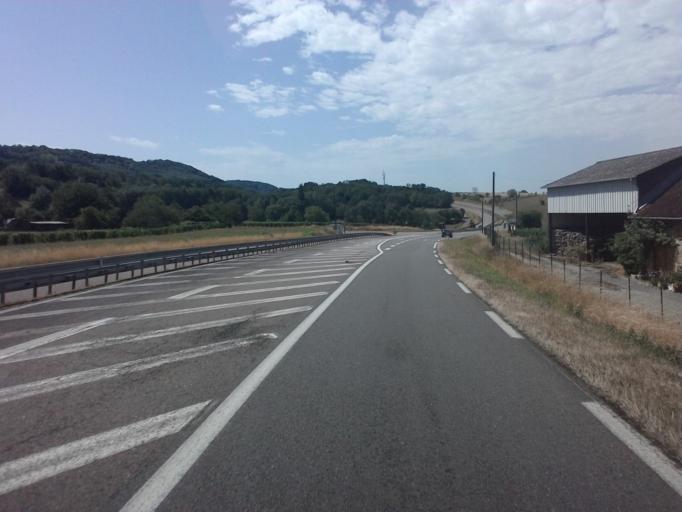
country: FR
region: Franche-Comte
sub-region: Departement du Jura
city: Cousance
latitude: 46.5567
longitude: 5.4077
